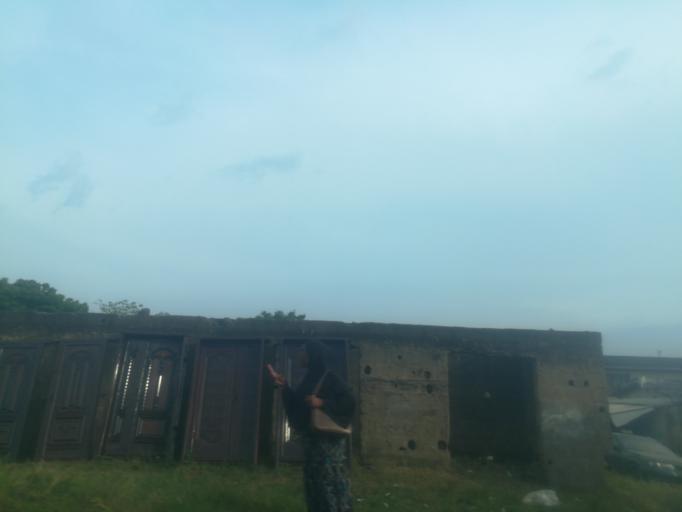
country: NG
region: Ogun
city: Abeokuta
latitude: 7.1612
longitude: 3.3122
